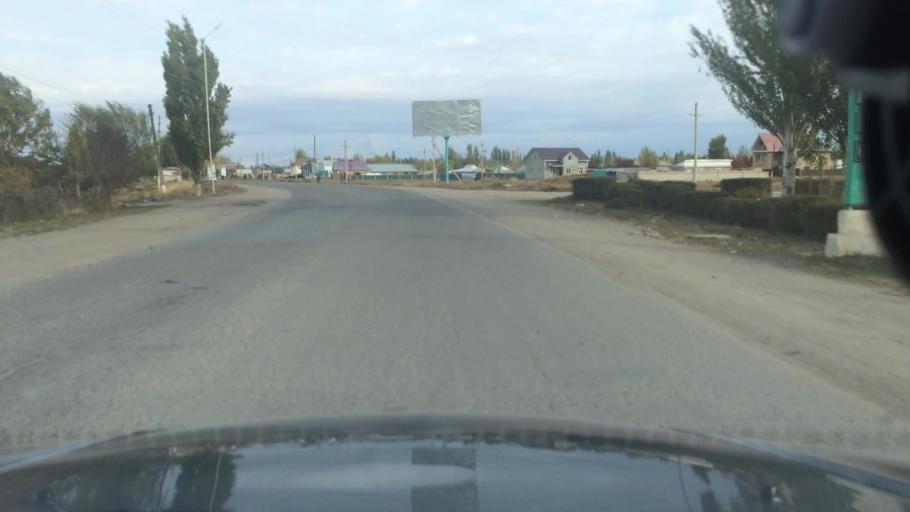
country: KG
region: Ysyk-Koel
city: Karakol
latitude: 42.5223
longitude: 78.3861
